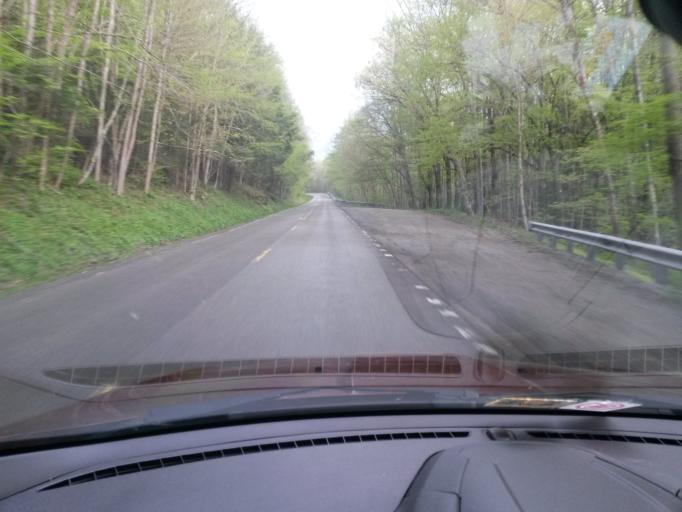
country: US
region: Virginia
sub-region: Highland County
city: Monterey
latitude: 38.5509
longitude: -79.7319
